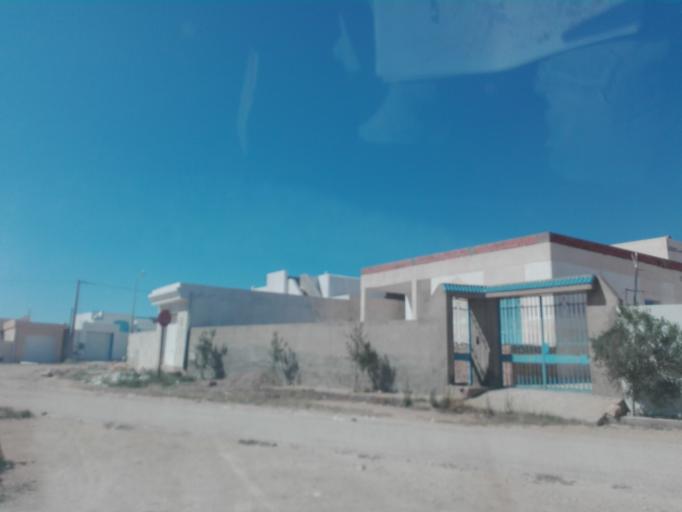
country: TN
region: Safaqis
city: Al Qarmadah
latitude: 34.7024
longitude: 11.1981
